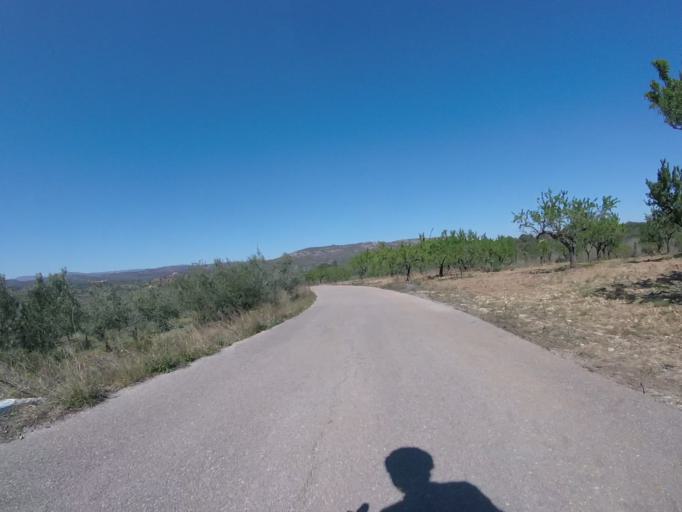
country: ES
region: Valencia
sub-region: Provincia de Castello
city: Cuevas de Vinroma
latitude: 40.3820
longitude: 0.1529
